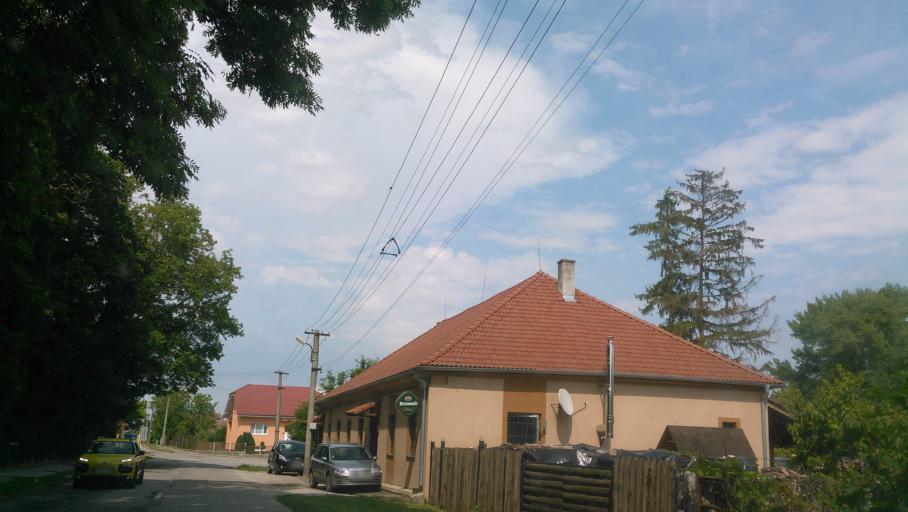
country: SK
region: Nitriansky
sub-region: Okres Nitra
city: Nitra
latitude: 48.4947
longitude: 18.0497
